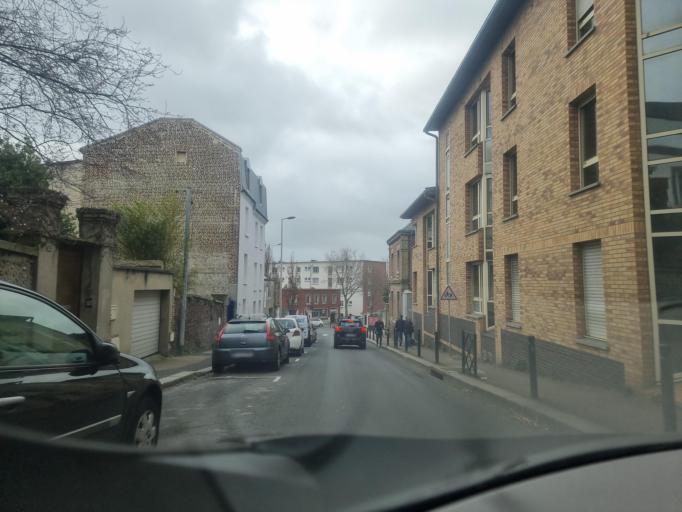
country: FR
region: Haute-Normandie
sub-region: Departement de la Seine-Maritime
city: Le Havre
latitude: 49.4975
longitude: 0.1005
